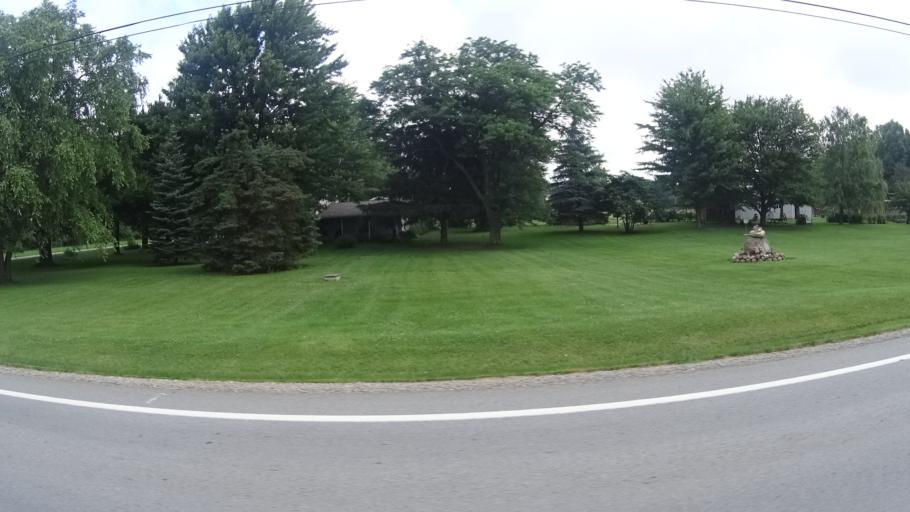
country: US
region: Ohio
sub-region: Huron County
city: Wakeman
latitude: 41.3055
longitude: -82.4809
